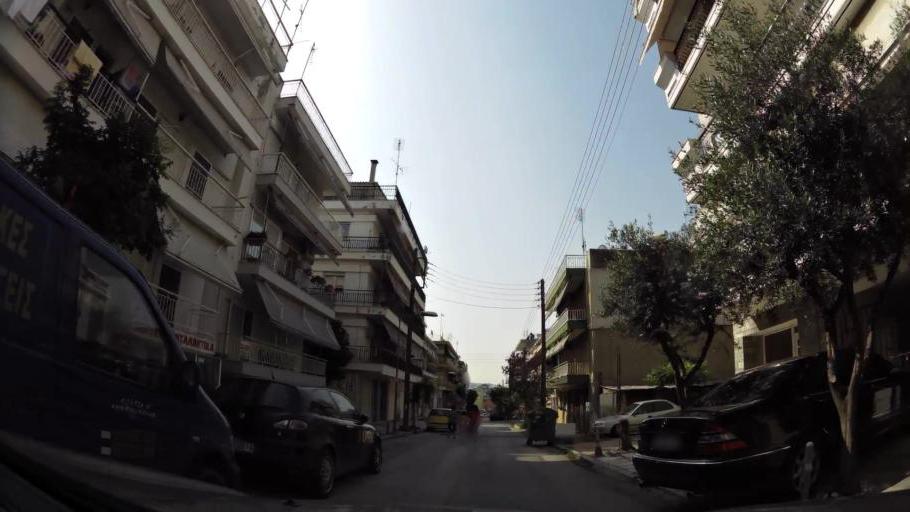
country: GR
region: Central Macedonia
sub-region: Nomos Thessalonikis
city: Stavroupoli
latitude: 40.6728
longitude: 22.9305
